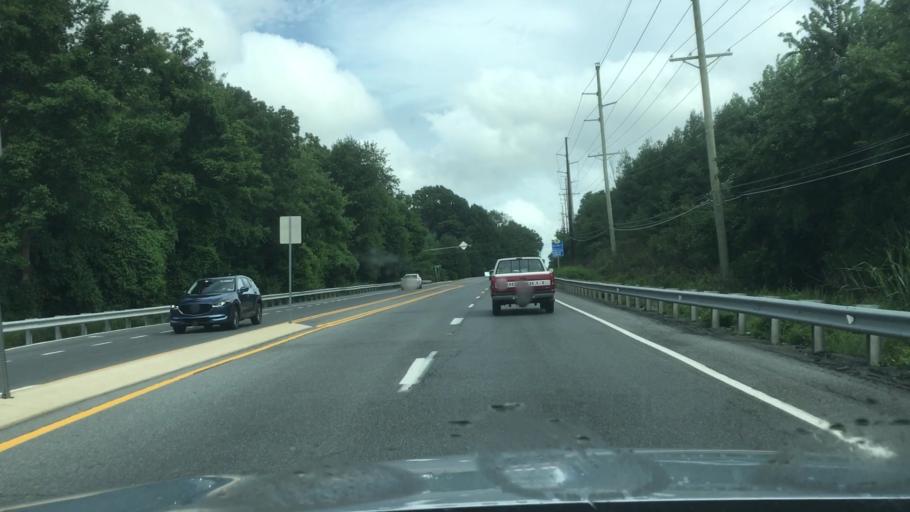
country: US
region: Delaware
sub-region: New Castle County
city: North Star
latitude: 39.7716
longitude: -75.7117
